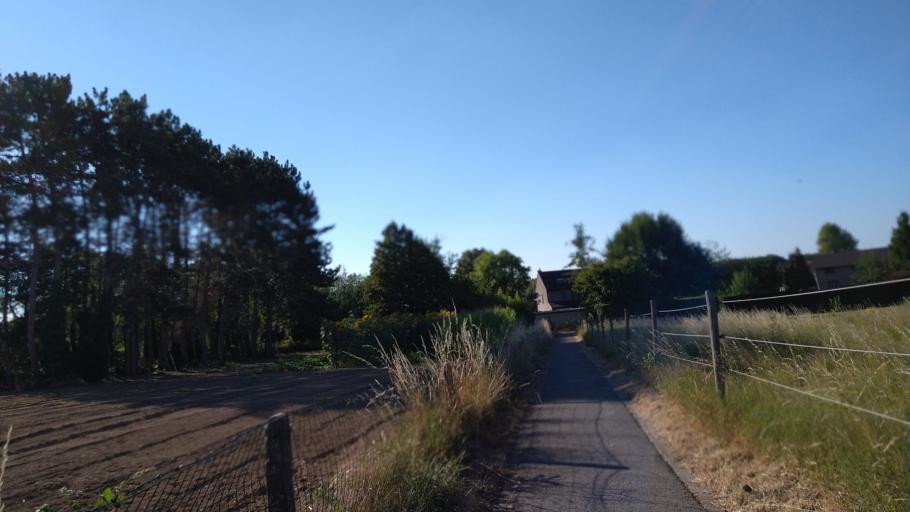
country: BE
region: Flanders
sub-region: Provincie Vlaams-Brabant
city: Bierbeek
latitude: 50.8744
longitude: 4.7577
